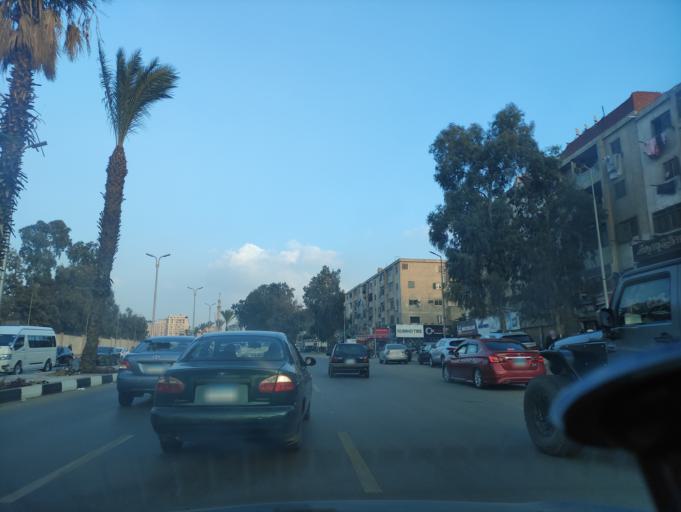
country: EG
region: Muhafazat al Qahirah
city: Cairo
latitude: 30.0501
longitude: 31.3169
